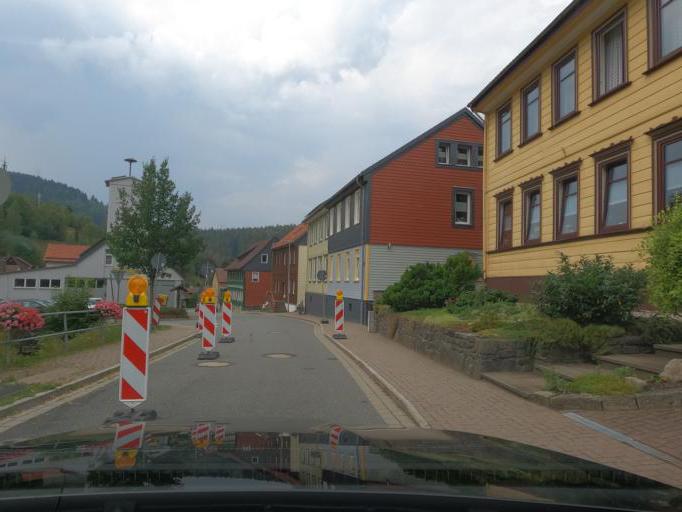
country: DE
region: Lower Saxony
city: Wildemann
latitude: 51.8666
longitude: 10.2910
